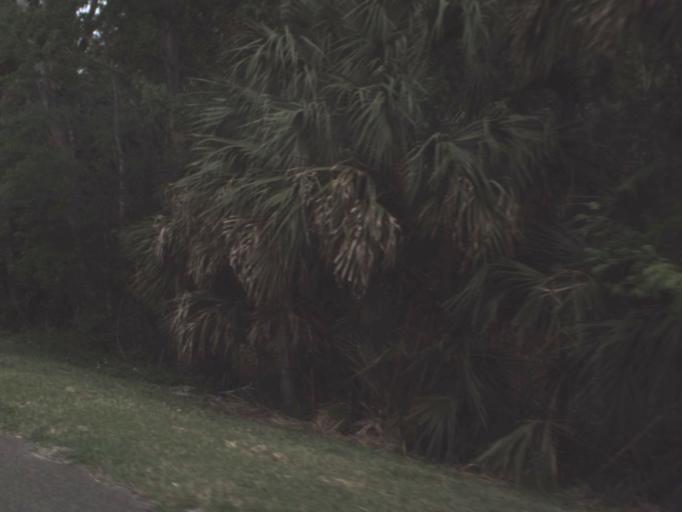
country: US
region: Florida
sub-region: Flagler County
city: Bunnell
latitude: 29.4166
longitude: -81.3033
